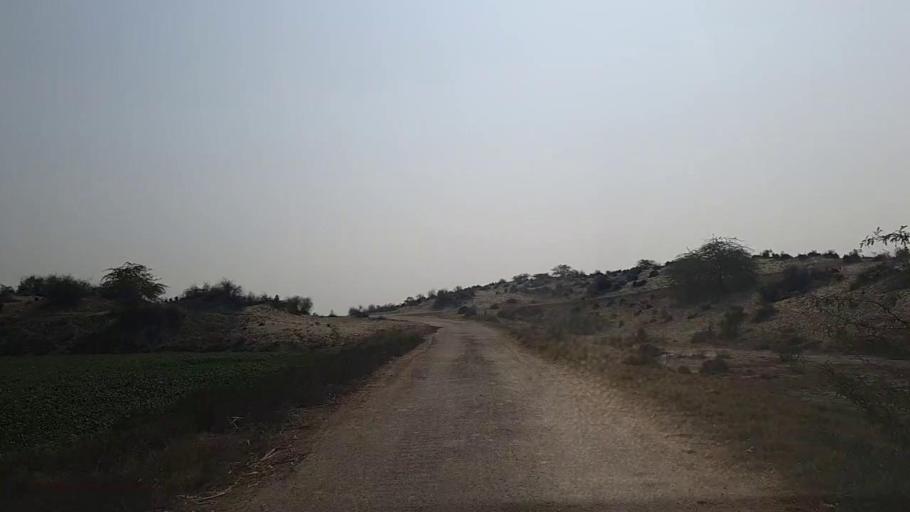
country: PK
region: Sindh
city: Jam Sahib
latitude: 26.4459
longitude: 68.5233
